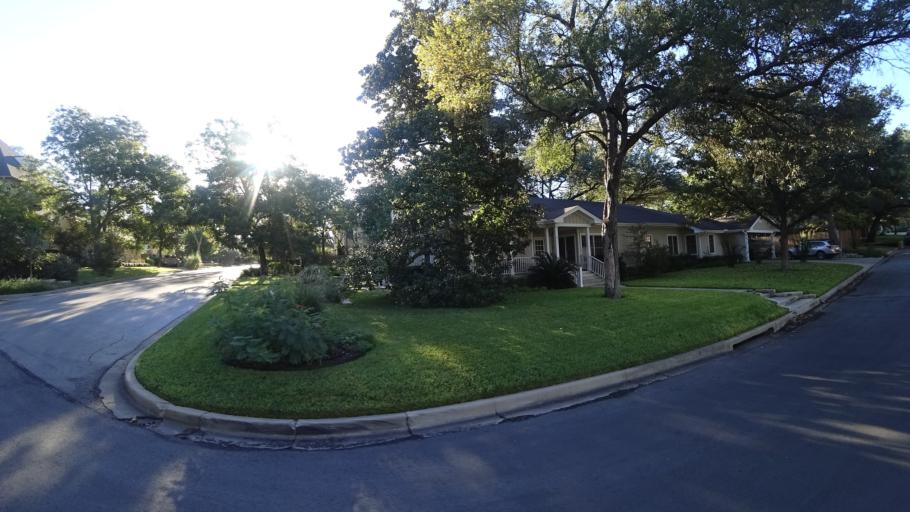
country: US
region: Texas
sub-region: Travis County
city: West Lake Hills
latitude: 30.2972
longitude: -97.7797
